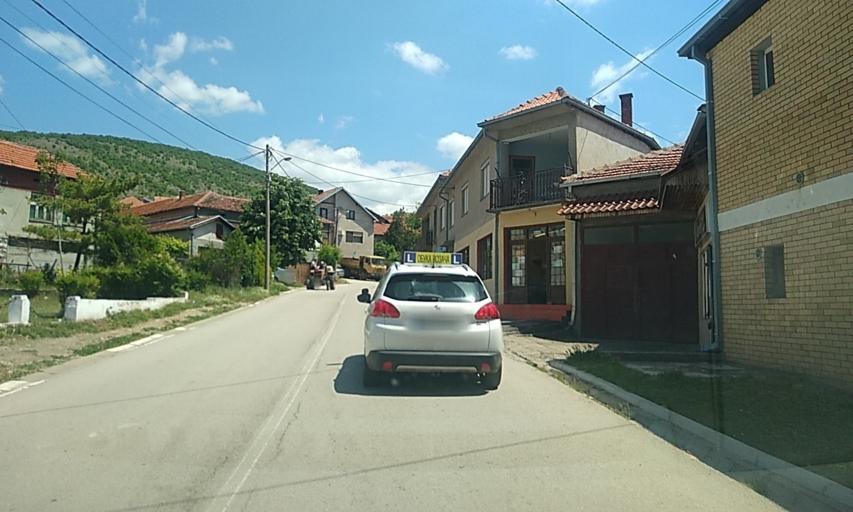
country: RS
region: Central Serbia
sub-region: Nisavski Okrug
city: Nis
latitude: 43.3638
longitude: 21.9681
